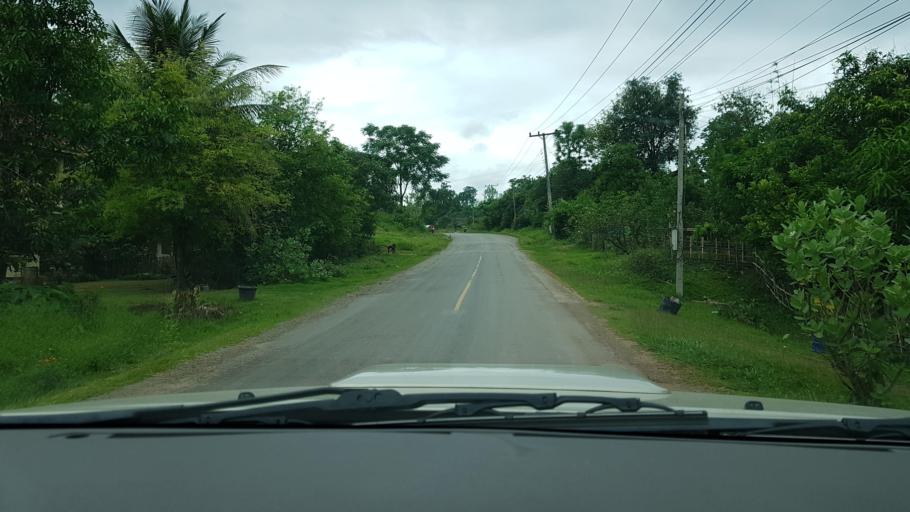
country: LA
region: Loungnamtha
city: Muang Nale
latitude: 20.3111
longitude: 101.6516
